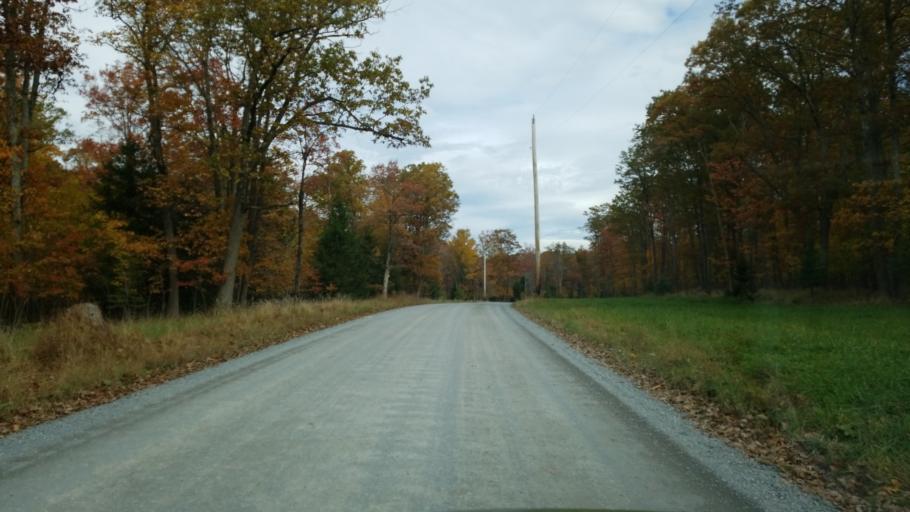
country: US
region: Pennsylvania
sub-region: Clearfield County
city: Clearfield
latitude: 41.1587
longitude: -78.4562
